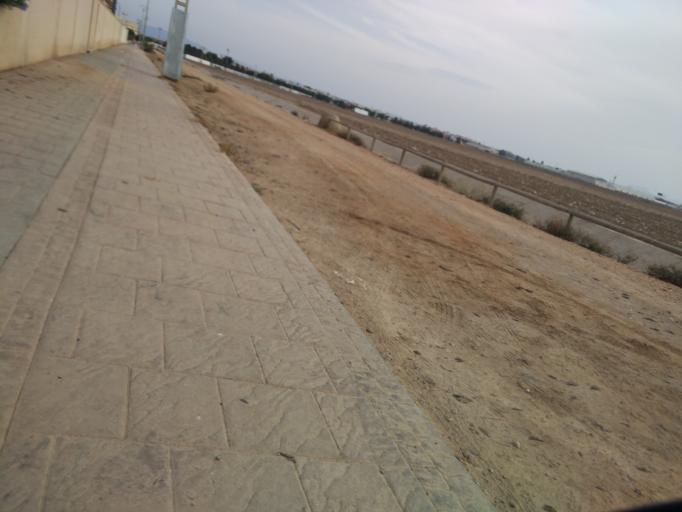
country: ES
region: Murcia
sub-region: Murcia
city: Los Alcazares
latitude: 37.7448
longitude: -0.8585
